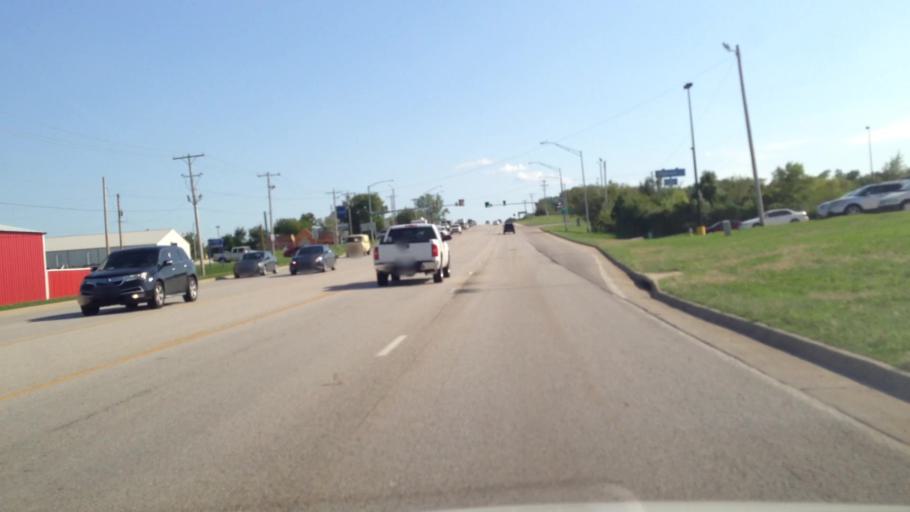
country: US
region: Kansas
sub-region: Bourbon County
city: Fort Scott
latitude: 37.8103
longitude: -94.7055
